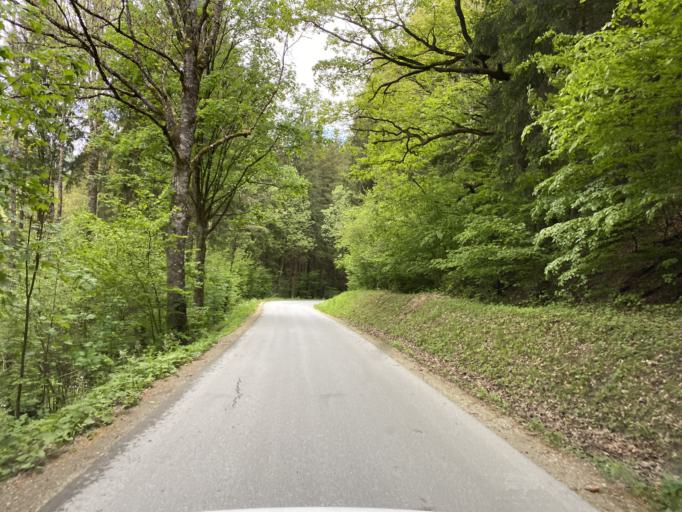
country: AT
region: Styria
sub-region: Politischer Bezirk Weiz
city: Koglhof
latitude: 47.3122
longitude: 15.6963
